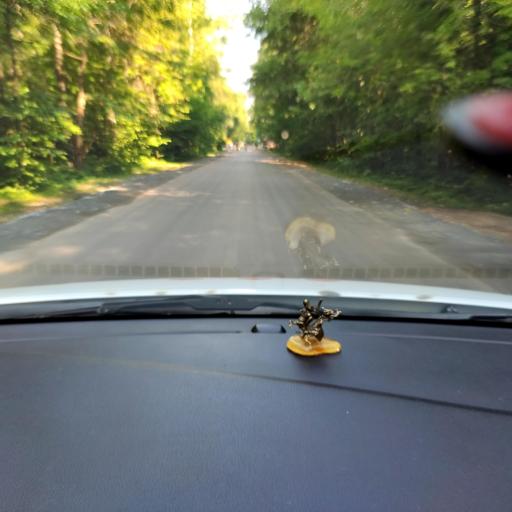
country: RU
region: Tatarstan
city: Stolbishchi
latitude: 55.7011
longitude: 49.2188
